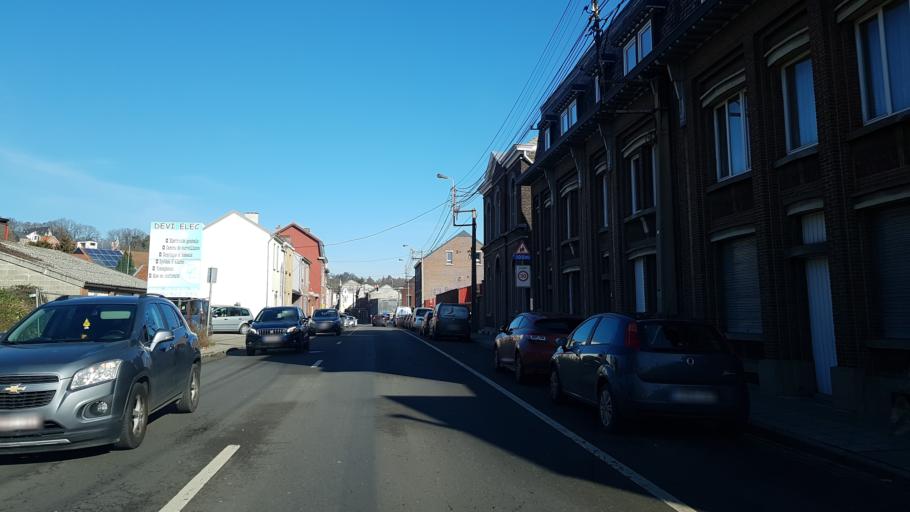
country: BE
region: Wallonia
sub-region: Province de Liege
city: Oupeye
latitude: 50.6946
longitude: 5.6489
